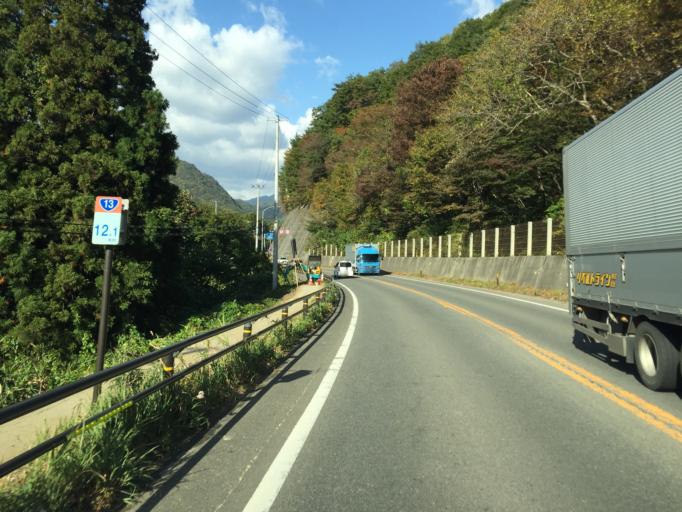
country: JP
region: Fukushima
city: Fukushima-shi
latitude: 37.8301
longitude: 140.3966
